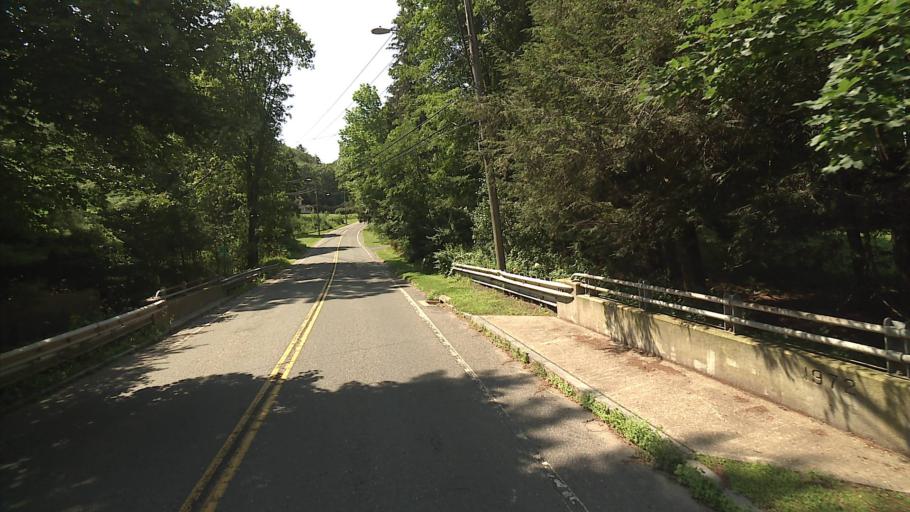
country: US
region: Connecticut
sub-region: Litchfield County
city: Winchester Center
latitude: 41.9866
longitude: -73.2003
